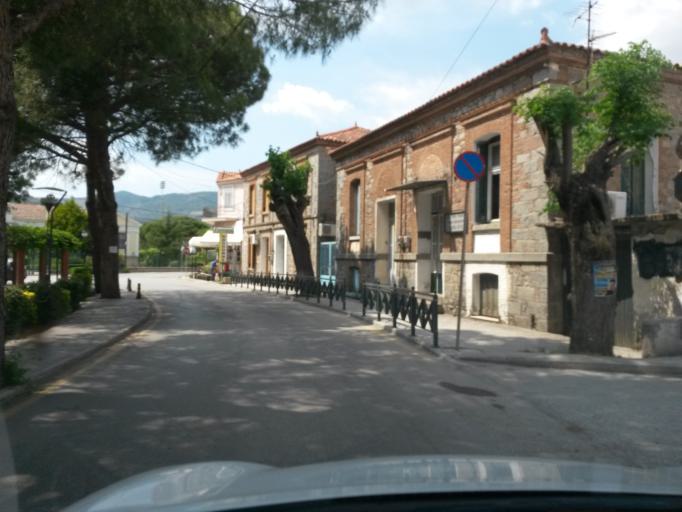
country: GR
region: North Aegean
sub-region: Nomos Lesvou
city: Kalloni
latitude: 39.2342
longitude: 26.2085
